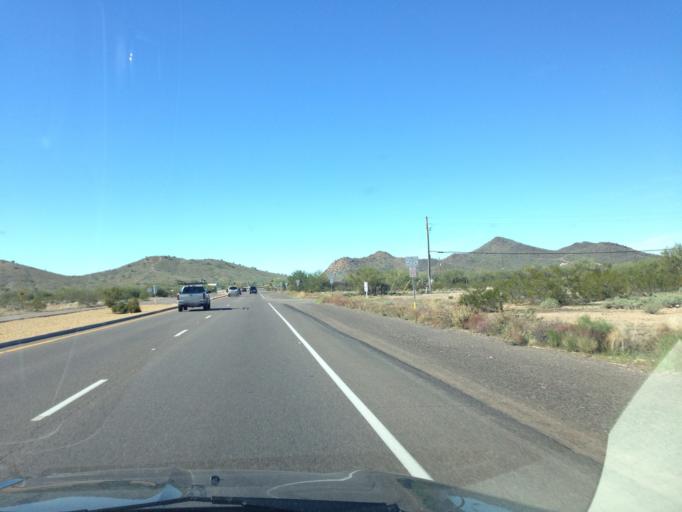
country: US
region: Arizona
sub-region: Maricopa County
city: Anthem
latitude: 33.7992
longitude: -112.0774
